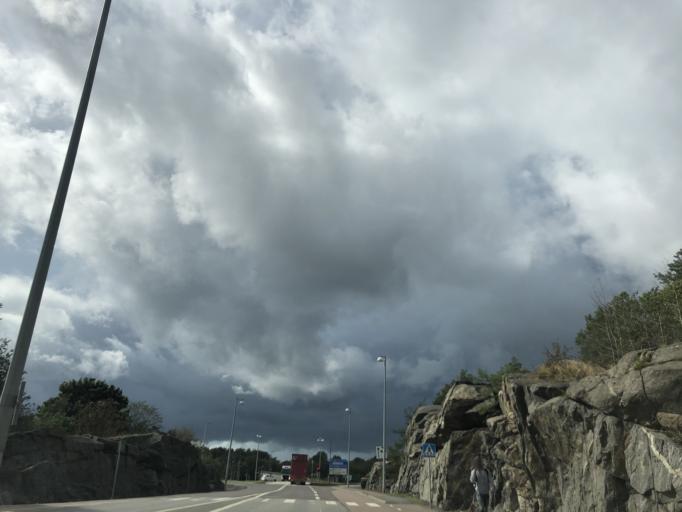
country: SE
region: Vaestra Goetaland
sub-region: Goteborg
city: Torslanda
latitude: 57.7188
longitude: 11.8236
